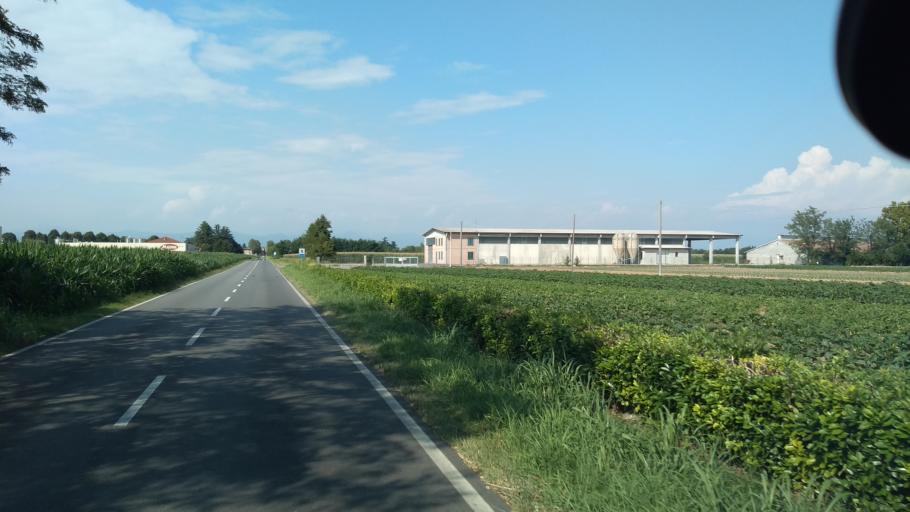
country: IT
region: Lombardy
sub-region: Provincia di Bergamo
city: Castel Rozzone
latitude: 45.5593
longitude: 9.6078
